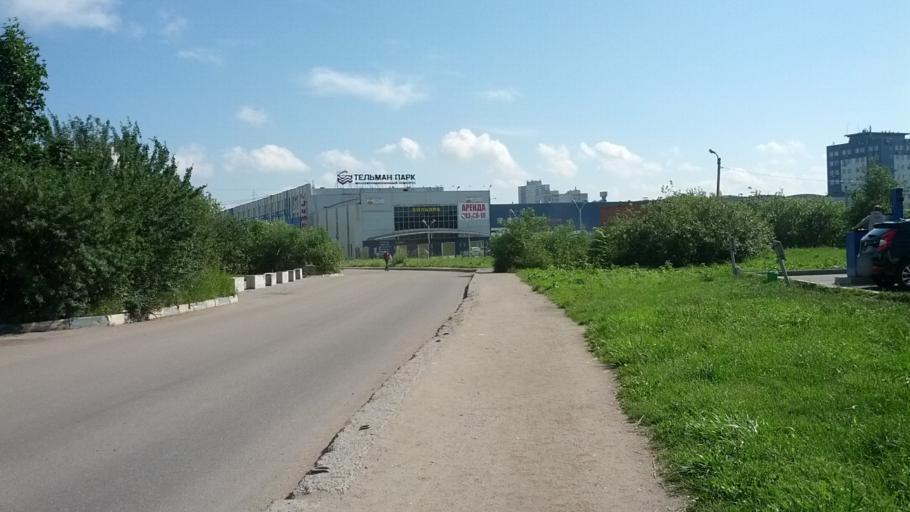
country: RU
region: Leningrad
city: Rybatskoye
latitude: 59.8912
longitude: 30.4817
